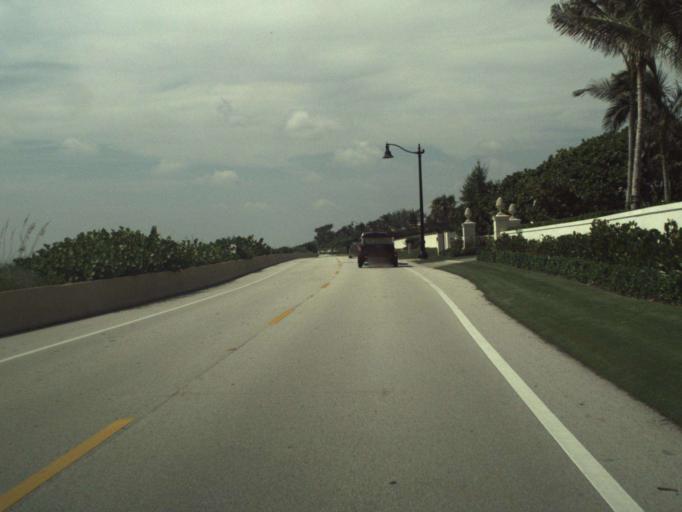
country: US
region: Florida
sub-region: Palm Beach County
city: Lake Clarke Shores
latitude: 26.6525
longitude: -80.0371
